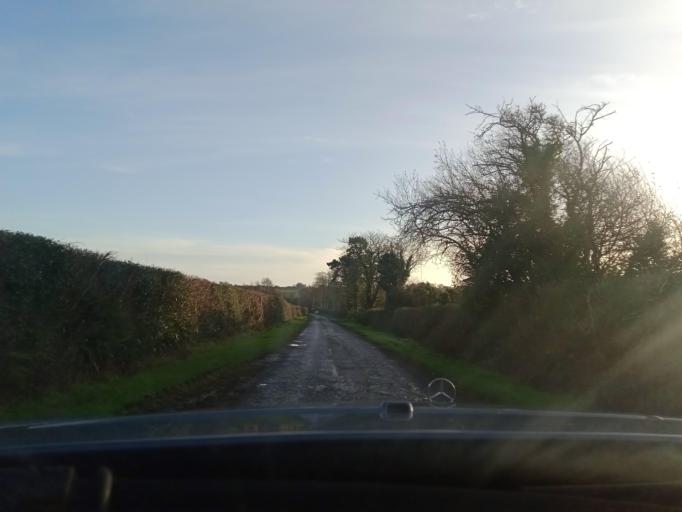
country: IE
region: Leinster
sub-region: Kilkenny
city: Callan
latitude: 52.4773
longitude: -7.4565
